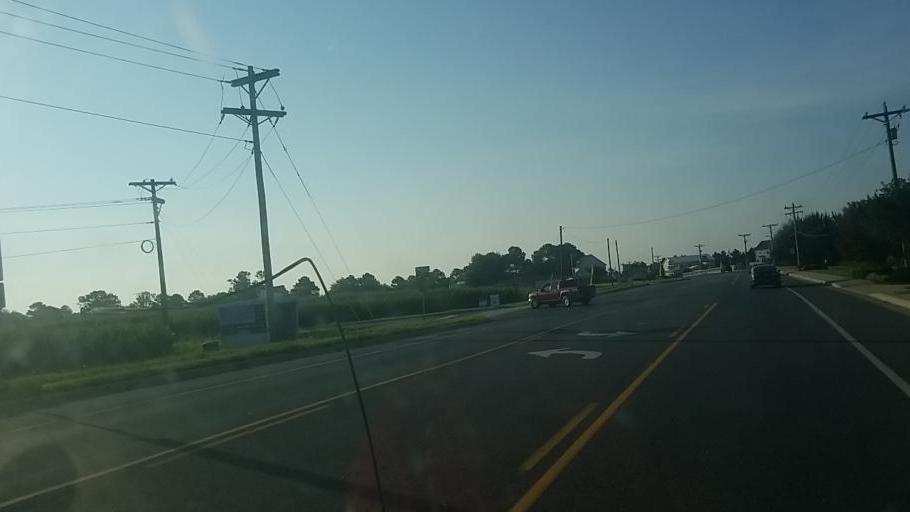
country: US
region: Delaware
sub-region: Sussex County
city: Ocean View
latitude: 38.4686
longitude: -75.0902
